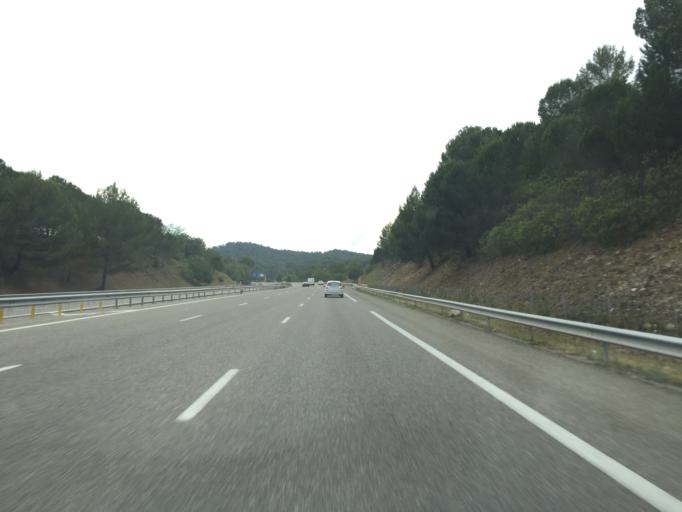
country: FR
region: Provence-Alpes-Cote d'Azur
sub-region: Departement du Var
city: Le Val
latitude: 43.4202
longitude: 6.0792
